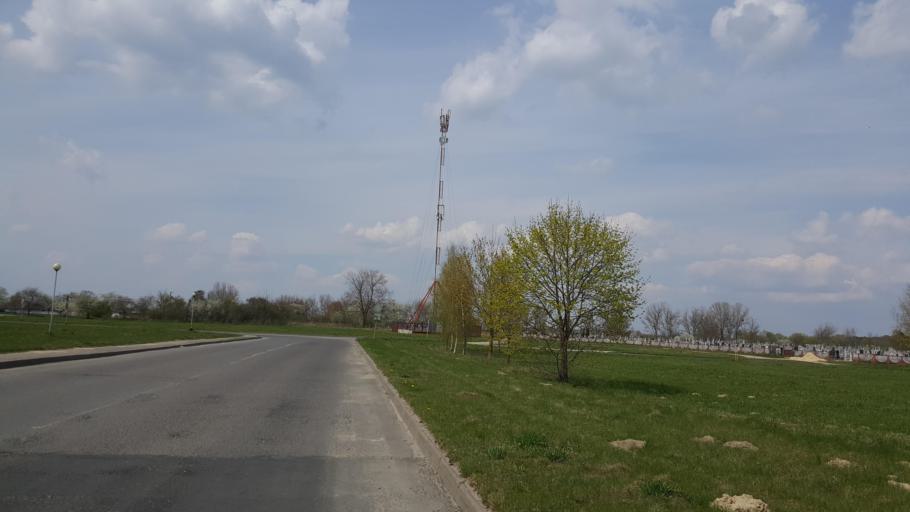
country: BY
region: Brest
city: Zhabinka
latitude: 52.1933
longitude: 23.9885
